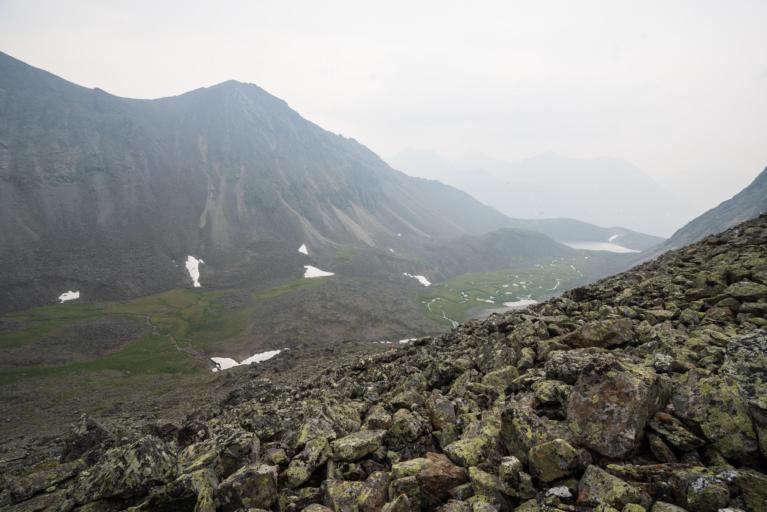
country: RU
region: Transbaikal Territory
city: Kuanda
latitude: 56.8060
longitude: 117.1136
